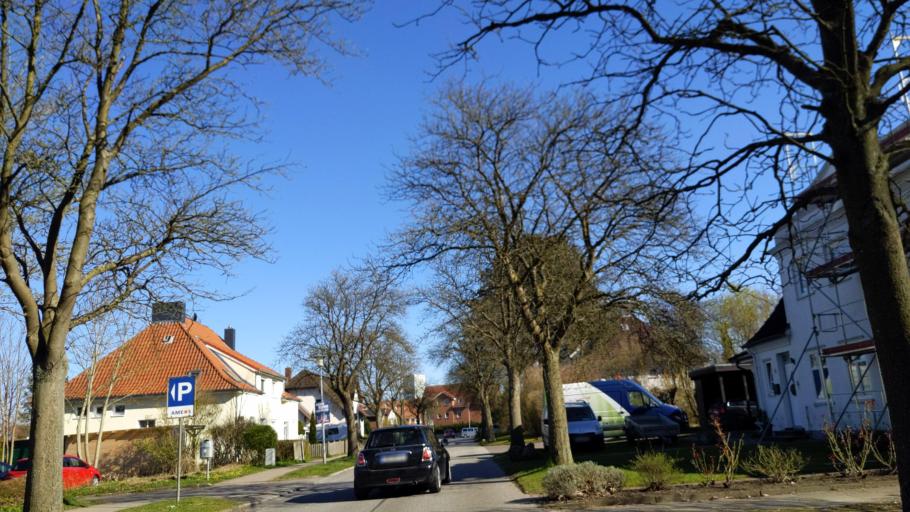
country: DE
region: Schleswig-Holstein
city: Neustadt in Holstein
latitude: 54.1044
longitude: 10.8000
